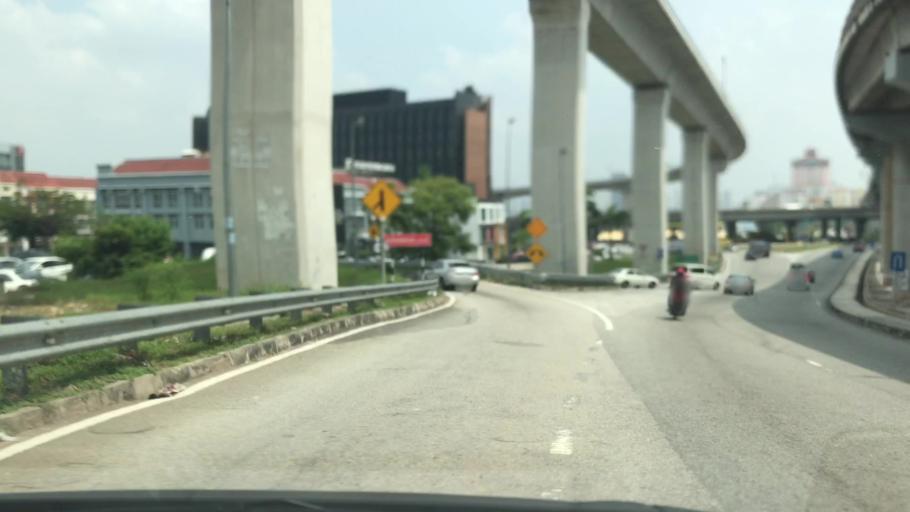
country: MY
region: Selangor
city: Subang Jaya
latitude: 3.0503
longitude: 101.6256
